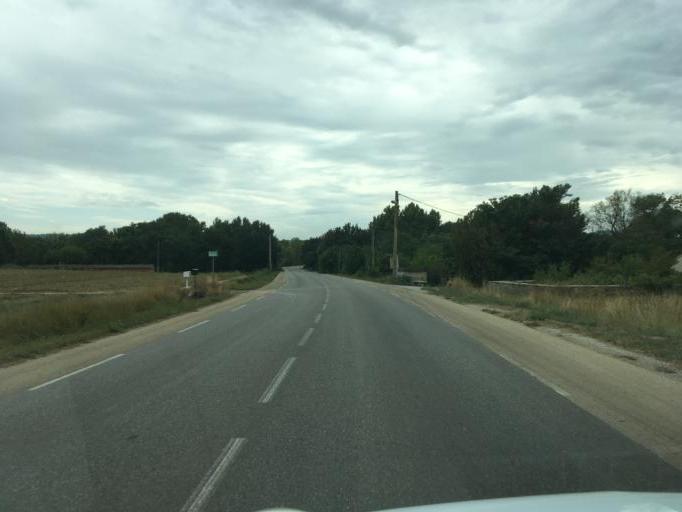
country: FR
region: Provence-Alpes-Cote d'Azur
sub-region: Departement des Bouches-du-Rhone
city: Rousset
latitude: 43.4737
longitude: 5.6179
